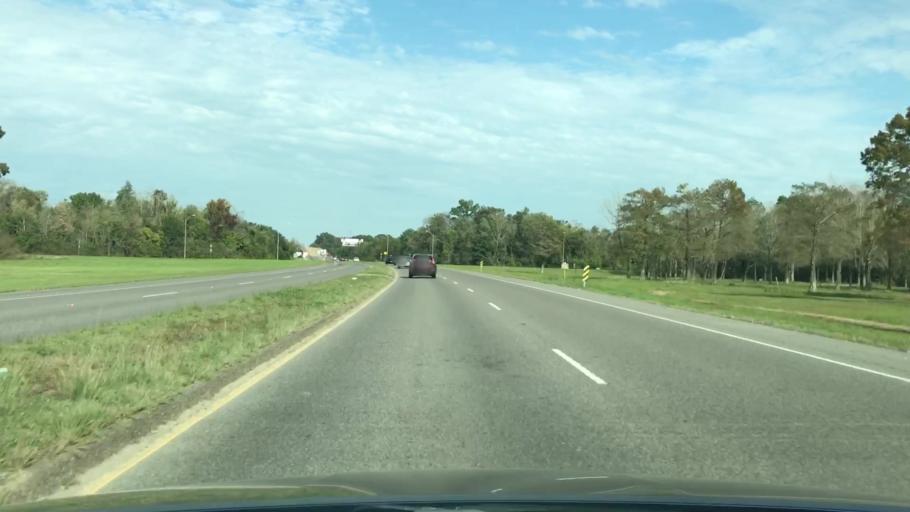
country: US
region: Louisiana
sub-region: Jefferson Parish
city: Bridge City
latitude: 29.9115
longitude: -90.1788
